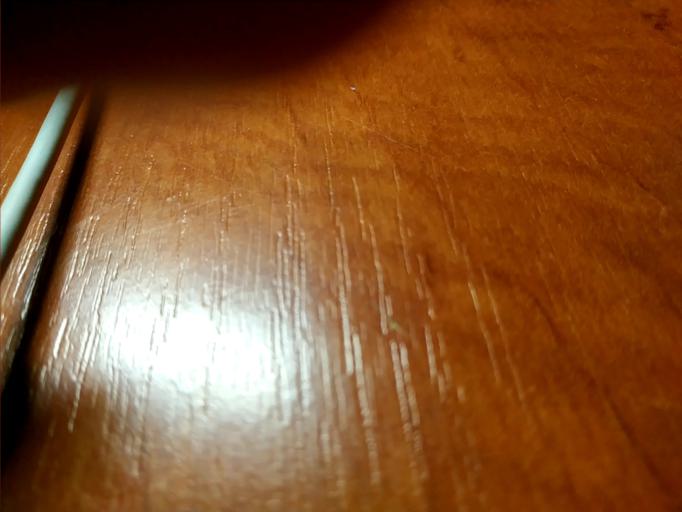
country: RU
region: Orjol
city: Naryshkino
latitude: 52.9756
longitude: 35.7064
